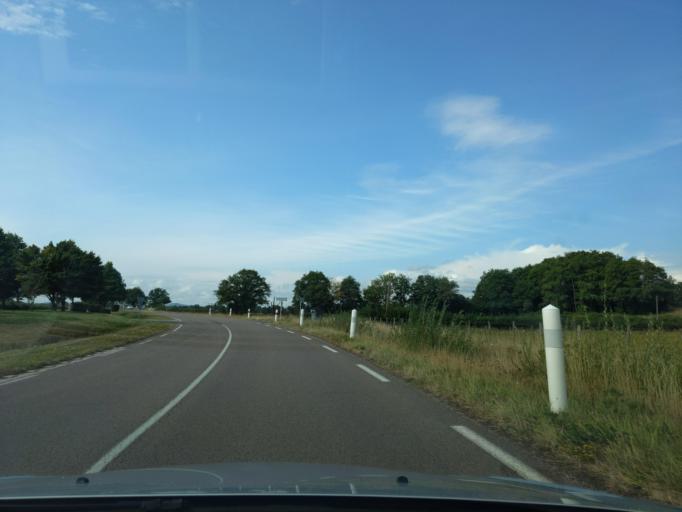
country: FR
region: Bourgogne
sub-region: Departement de Saone-et-Loire
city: Etang-sur-Arroux
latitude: 46.9322
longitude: 4.2081
